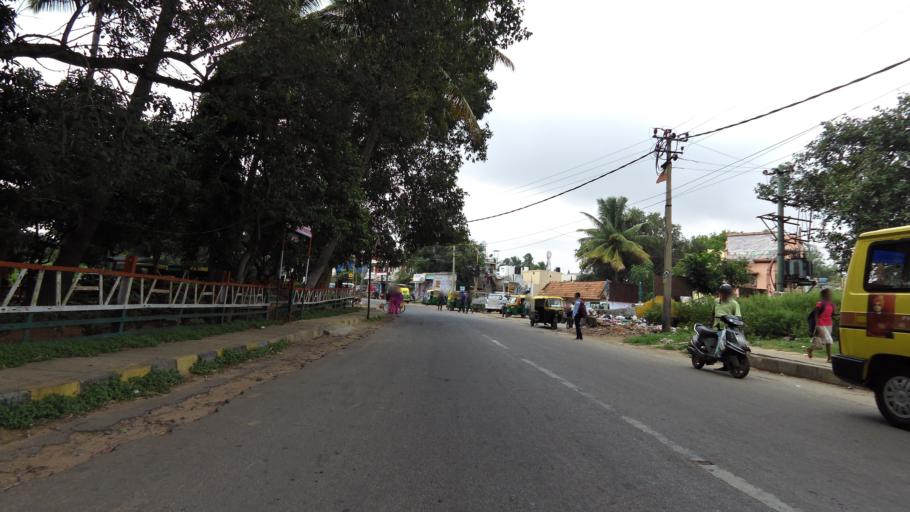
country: IN
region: Karnataka
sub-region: Bangalore Urban
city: Bangalore
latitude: 12.9961
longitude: 77.6425
